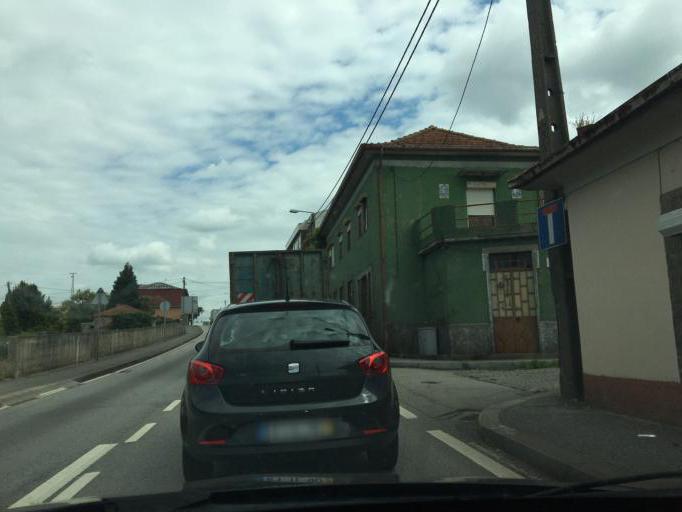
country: PT
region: Porto
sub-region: Maia
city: Anta
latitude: 41.2567
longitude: -8.6163
